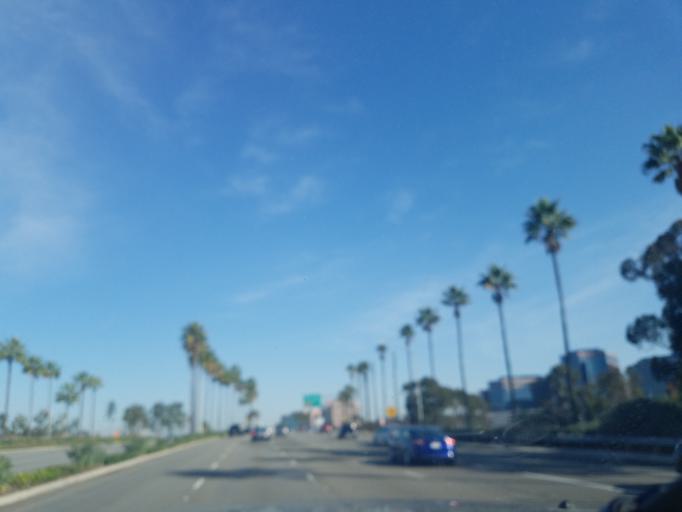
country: US
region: California
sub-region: Orange County
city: Irvine
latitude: 33.6808
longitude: -117.8584
